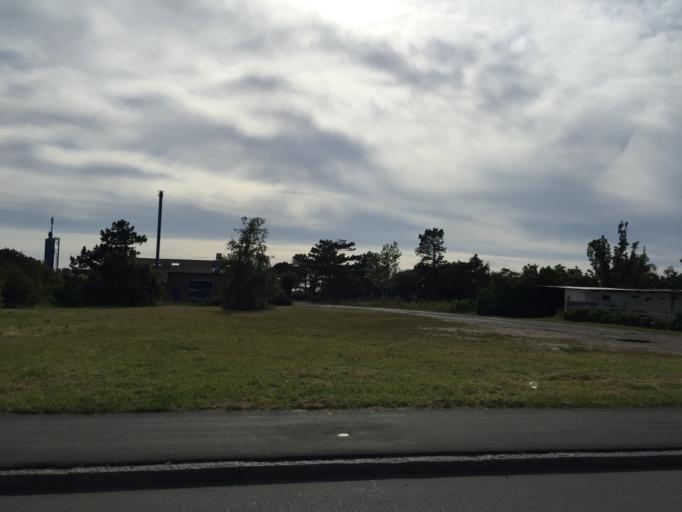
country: DK
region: Capital Region
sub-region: Halsnaes Kommune
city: Hundested
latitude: 55.9554
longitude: 11.8545
